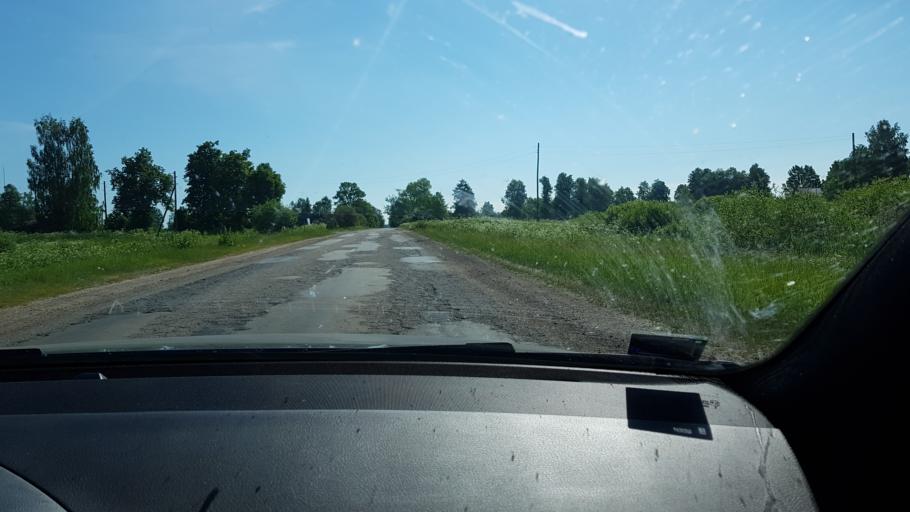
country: LV
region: Daugavpils
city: Daugavpils
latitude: 55.8215
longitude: 26.7640
